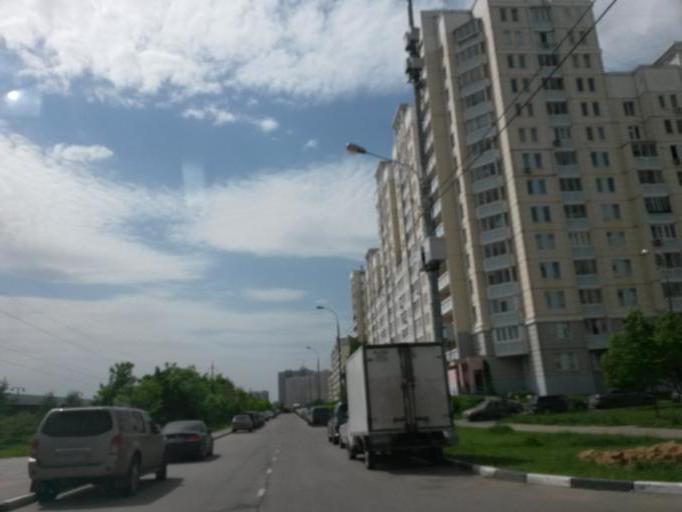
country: RU
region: Moskovskaya
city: Kommunarka
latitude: 55.5406
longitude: 37.5232
